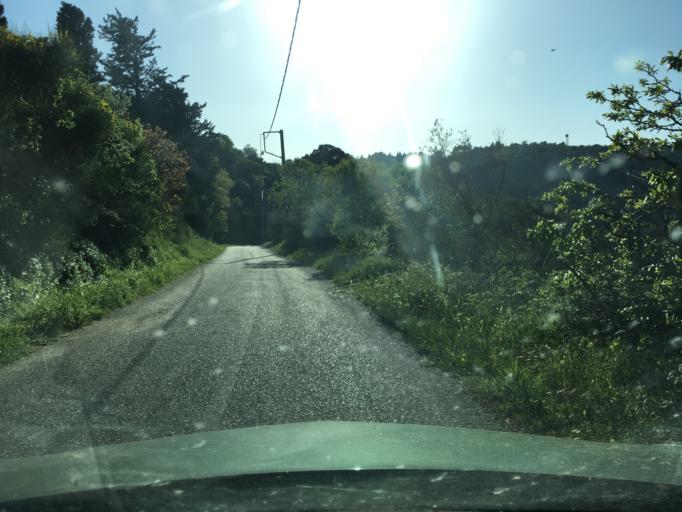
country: GR
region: Thessaly
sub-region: Nomos Magnisias
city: Skopelos
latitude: 39.1819
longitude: 23.6233
